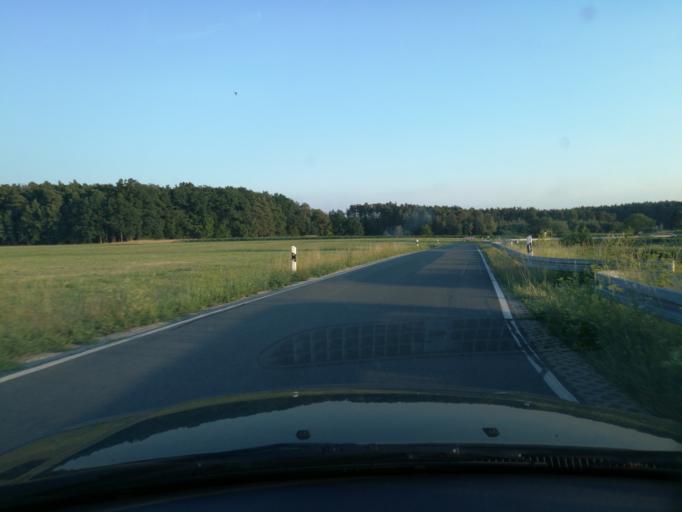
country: DE
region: Bavaria
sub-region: Regierungsbezirk Mittelfranken
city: Hessdorf
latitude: 49.6452
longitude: 10.9160
